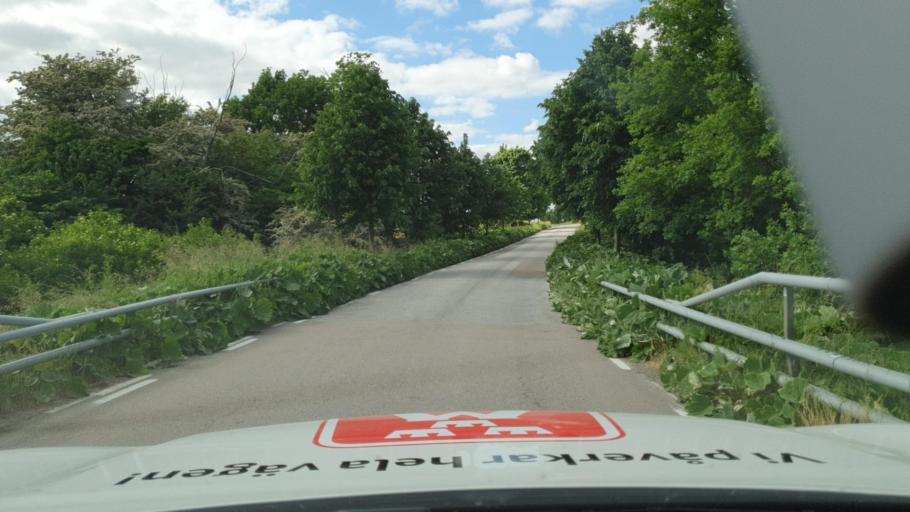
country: SE
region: Skane
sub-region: Ystads Kommun
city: Kopingebro
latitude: 55.4719
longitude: 13.9999
